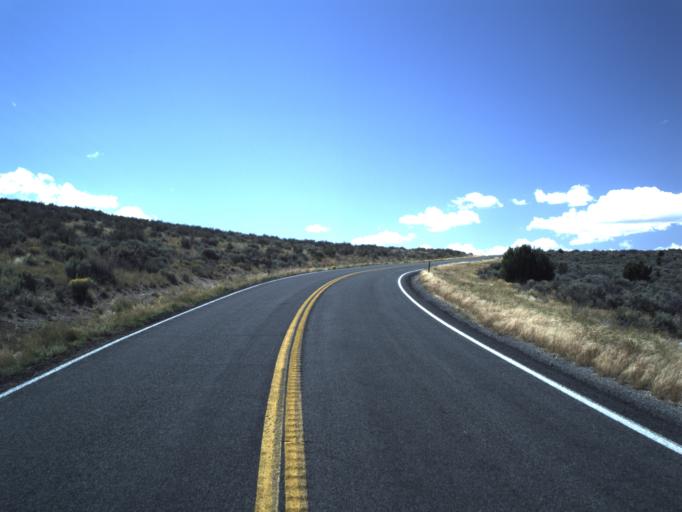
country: US
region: Utah
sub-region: Iron County
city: Parowan
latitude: 38.0755
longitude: -112.9582
